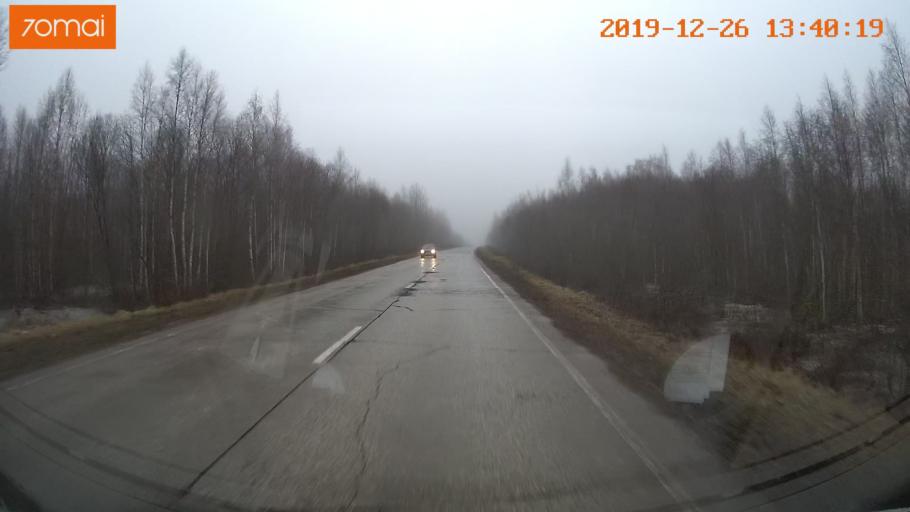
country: RU
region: Vologda
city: Sheksna
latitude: 58.7437
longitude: 38.4275
